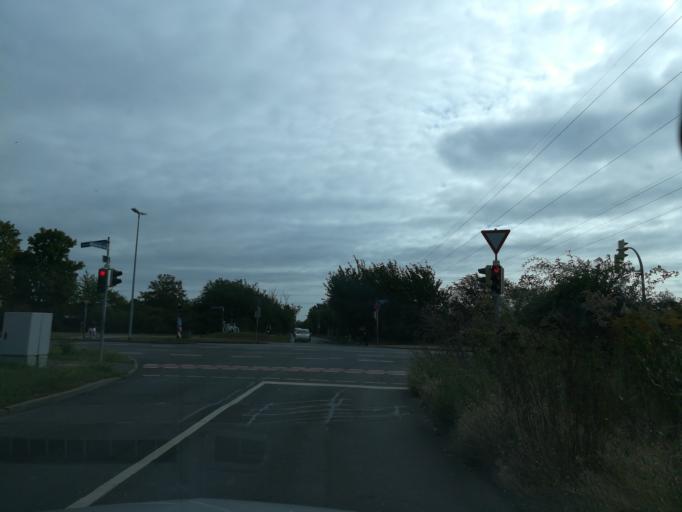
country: DE
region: Saxony-Anhalt
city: Neue Neustadt
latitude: 52.1584
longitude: 11.6027
